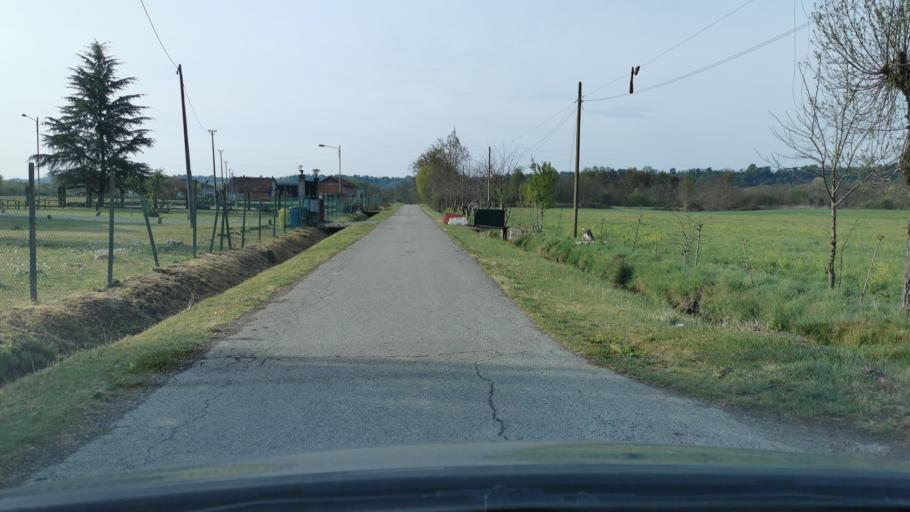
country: IT
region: Piedmont
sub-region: Provincia di Torino
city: Front
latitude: 45.2818
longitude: 7.6883
